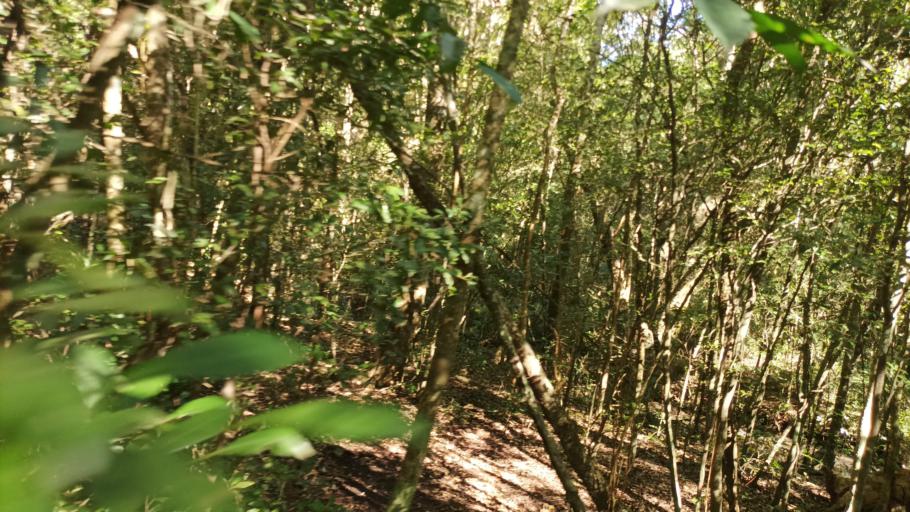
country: AR
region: Misiones
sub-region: Departamento de Candelaria
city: Candelaria
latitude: -27.5568
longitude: -55.7109
